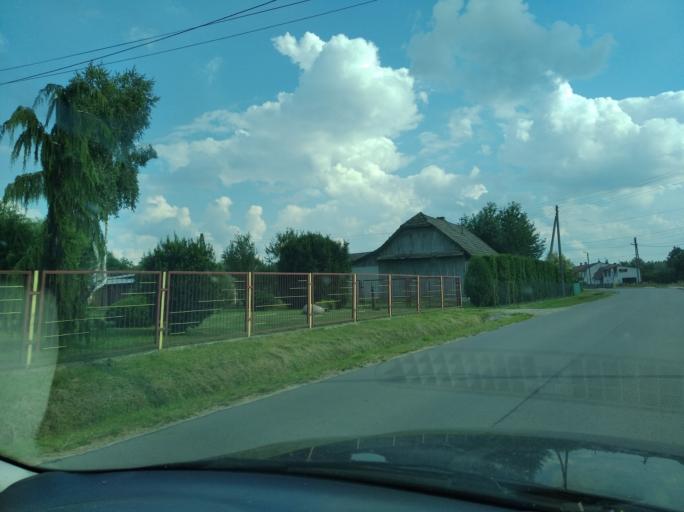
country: PL
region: Subcarpathian Voivodeship
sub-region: Powiat rzeszowski
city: Wysoka Glogowska
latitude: 50.1521
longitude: 22.0172
